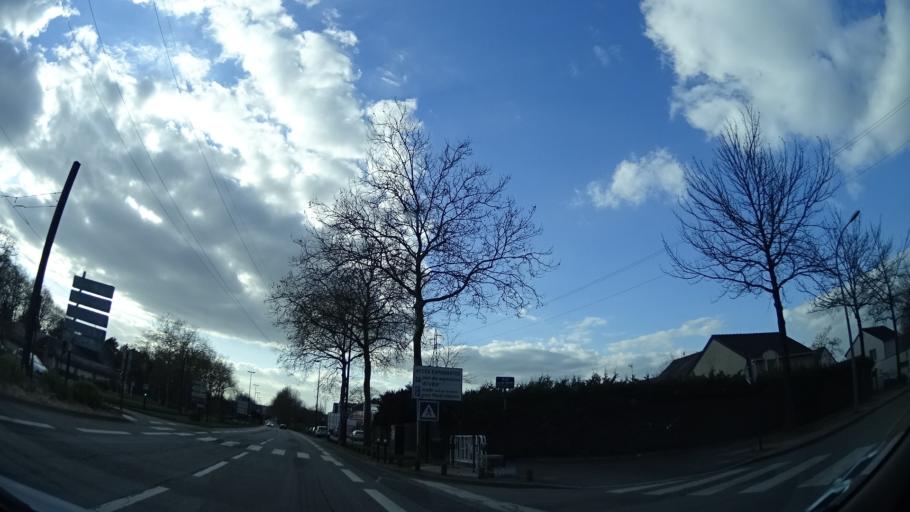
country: FR
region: Pays de la Loire
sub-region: Departement de la Loire-Atlantique
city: Sainte-Luce-sur-Loire
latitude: 47.2589
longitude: -1.5216
